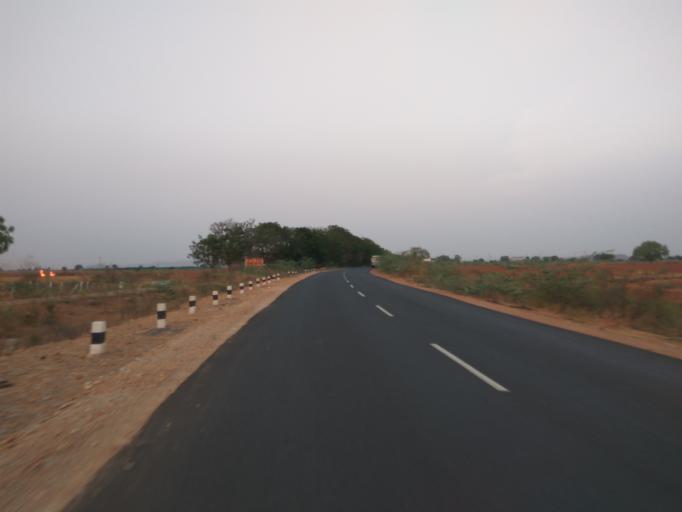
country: IN
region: Andhra Pradesh
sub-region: Prakasam
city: Markapur
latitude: 15.7505
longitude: 79.2185
